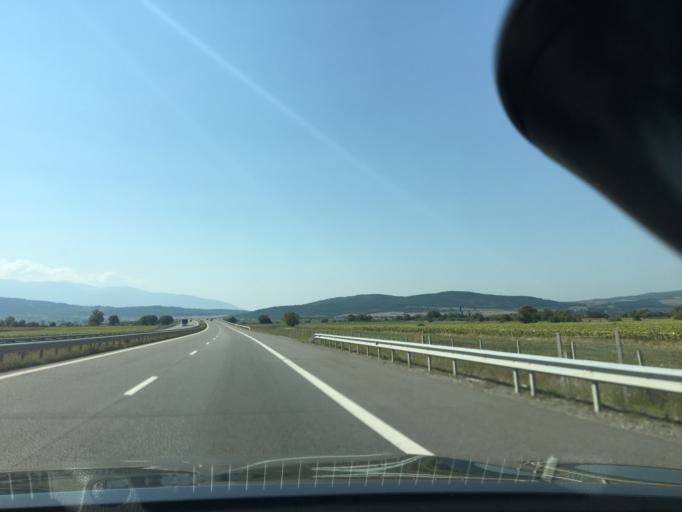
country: BG
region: Kyustendil
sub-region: Obshtina Bobovdol
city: Bobovdol
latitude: 42.4393
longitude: 23.1123
